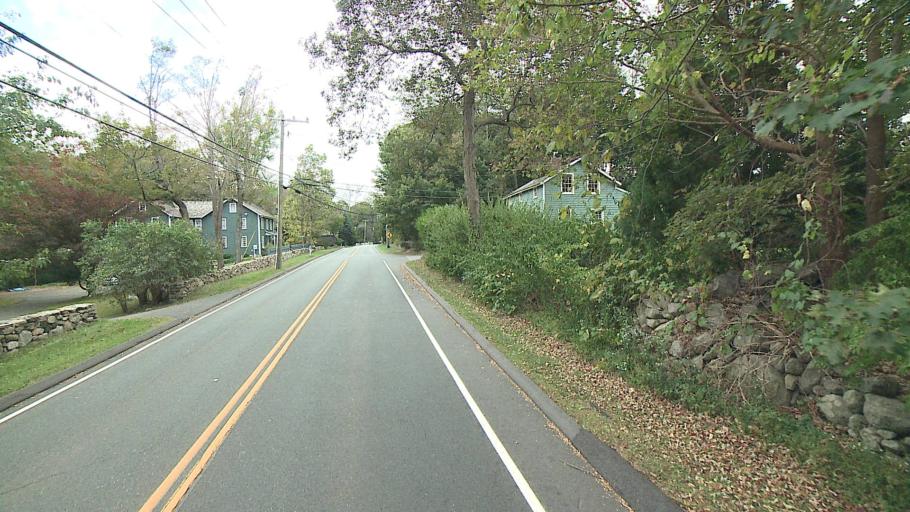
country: US
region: Connecticut
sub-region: Fairfield County
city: Georgetown
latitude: 41.2307
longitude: -73.4801
